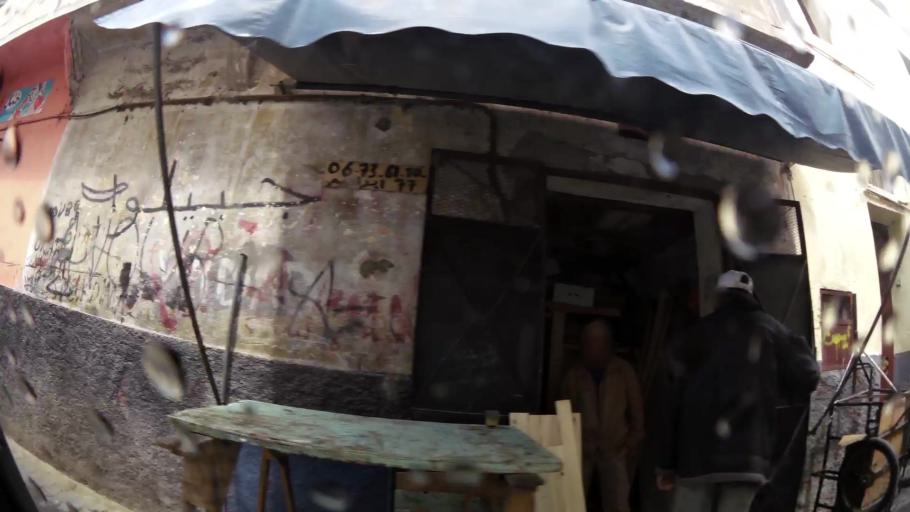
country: MA
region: Grand Casablanca
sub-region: Casablanca
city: Casablanca
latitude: 33.5742
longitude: -7.5933
